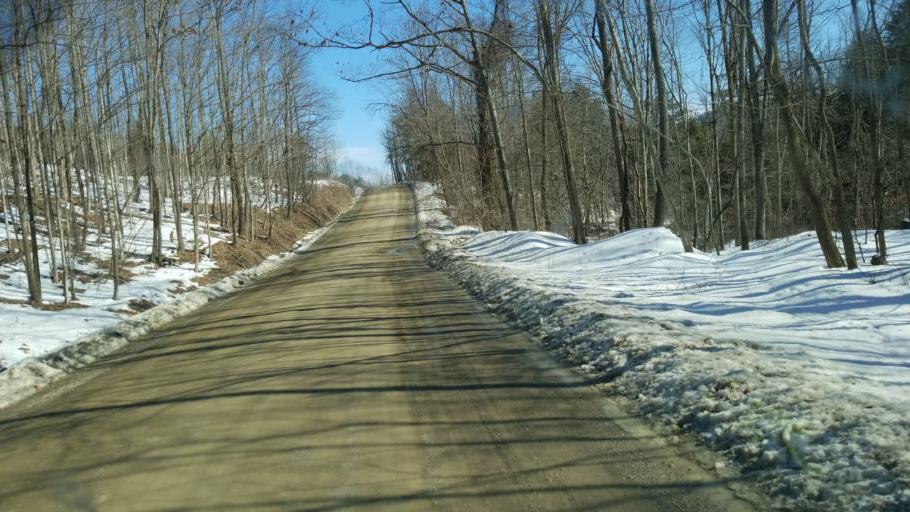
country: US
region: New York
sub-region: Allegany County
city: Alfred
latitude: 42.2479
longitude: -77.7052
